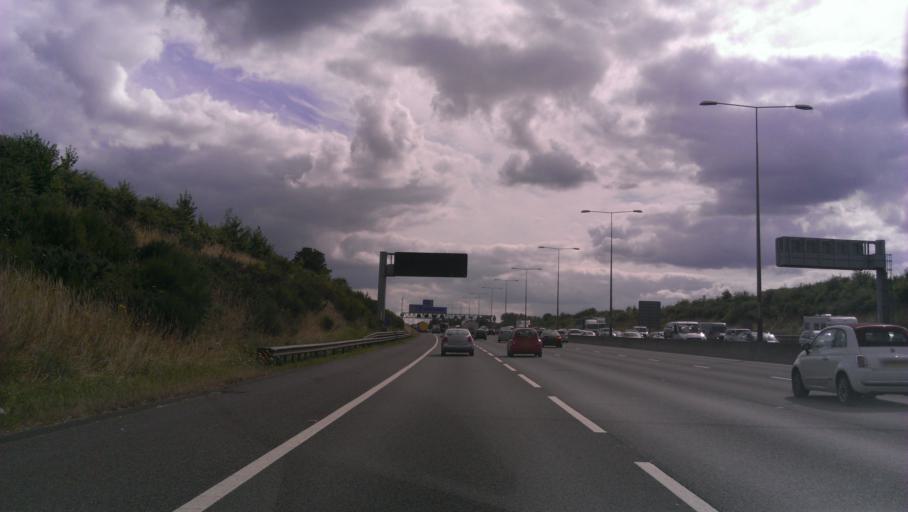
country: GB
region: England
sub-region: Kent
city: Dartford
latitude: 51.4101
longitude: 0.2161
